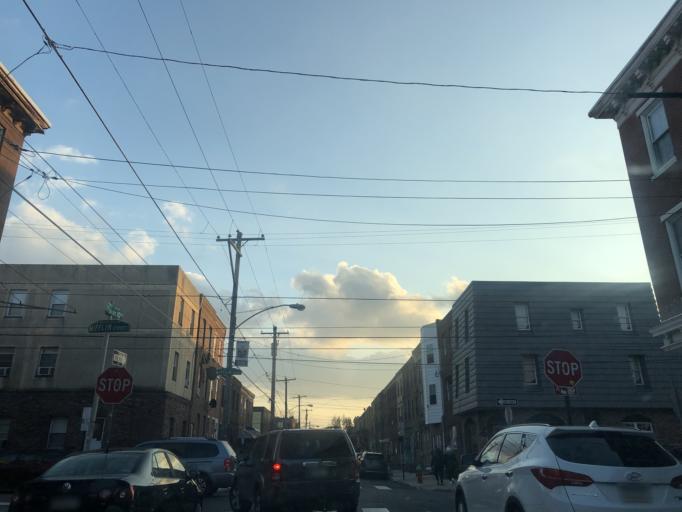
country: US
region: Pennsylvania
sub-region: Philadelphia County
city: Philadelphia
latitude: 39.9261
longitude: -75.1623
